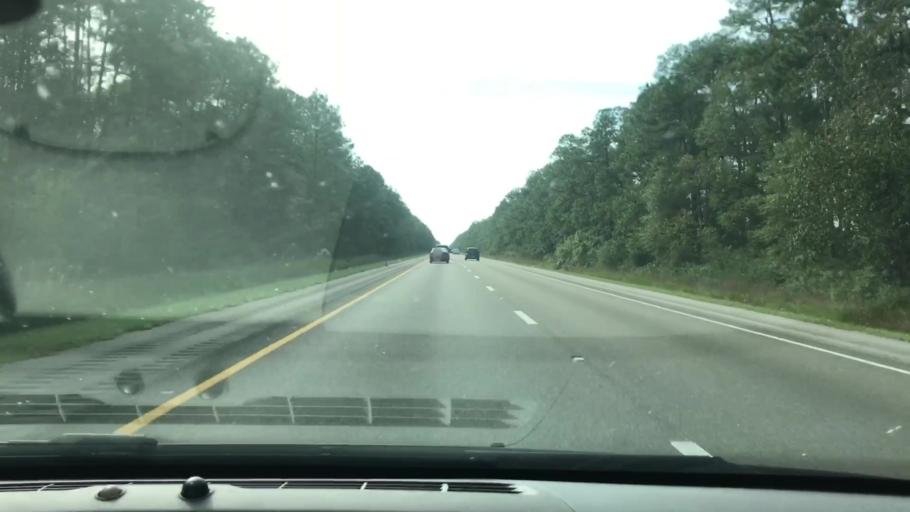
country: US
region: Mississippi
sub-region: Hancock County
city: Pearlington
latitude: 30.3284
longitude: -89.5586
